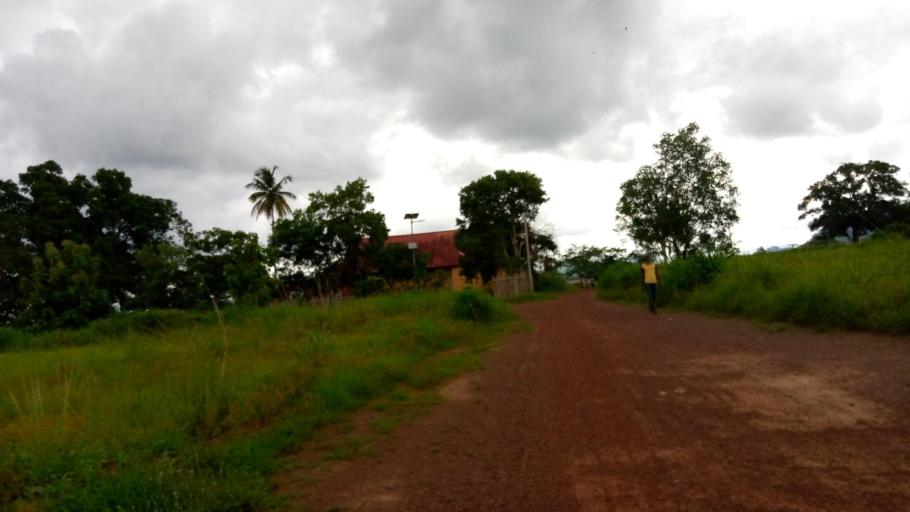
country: SL
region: Southern Province
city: Moyamba
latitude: 8.1602
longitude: -12.4439
